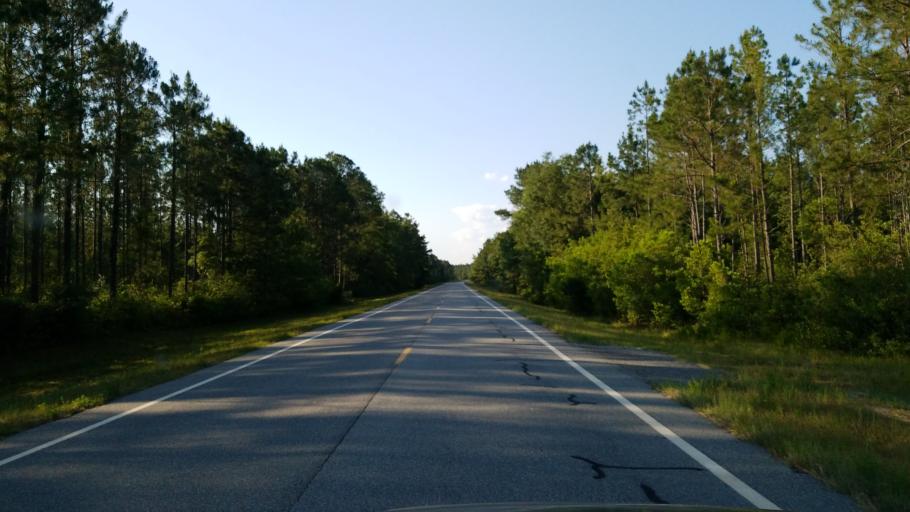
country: US
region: Georgia
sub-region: Lanier County
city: Lakeland
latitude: 30.8790
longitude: -83.0528
